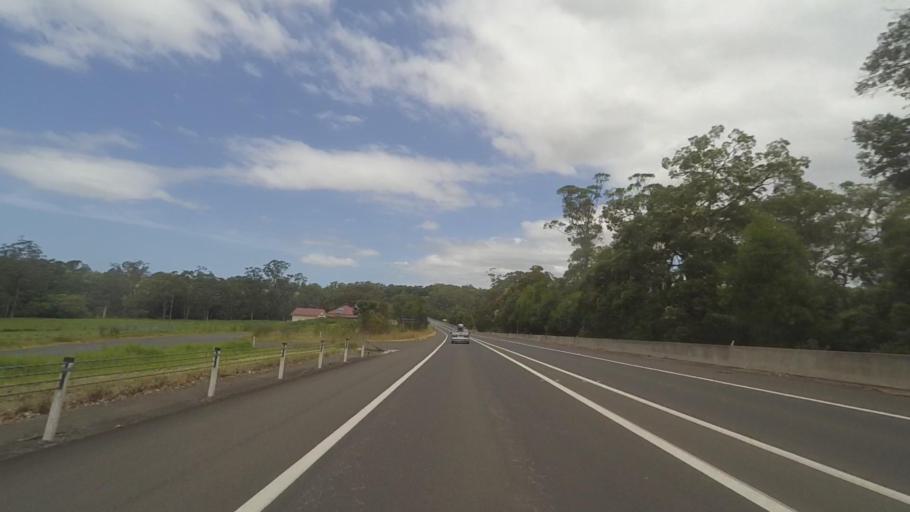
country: AU
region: New South Wales
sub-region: Shoalhaven Shire
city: Milton
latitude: -35.2125
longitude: 150.4359
